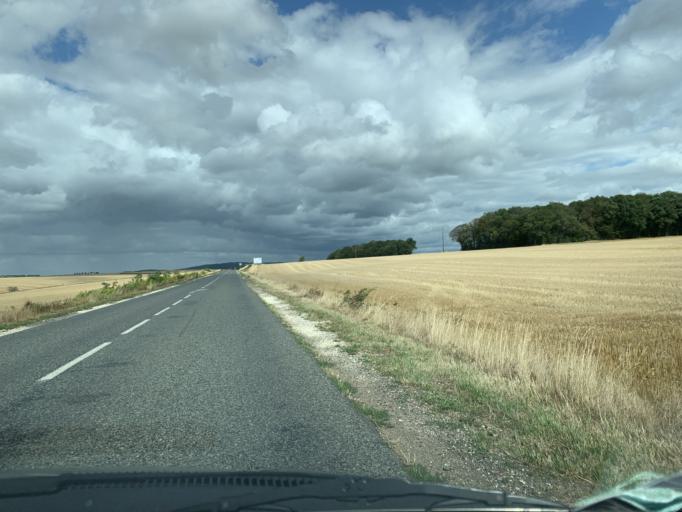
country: FR
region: Bourgogne
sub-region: Departement de la Nievre
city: Clamecy
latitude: 47.4269
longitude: 3.4744
